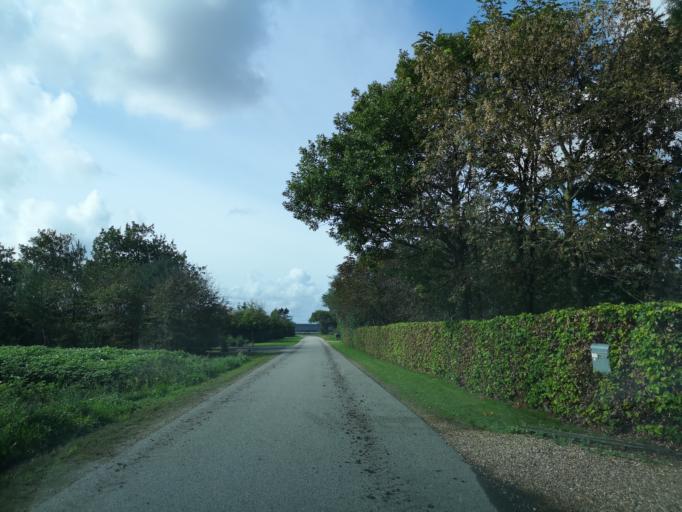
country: DK
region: Central Jutland
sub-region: Ringkobing-Skjern Kommune
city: Tarm
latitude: 55.9533
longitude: 8.5549
